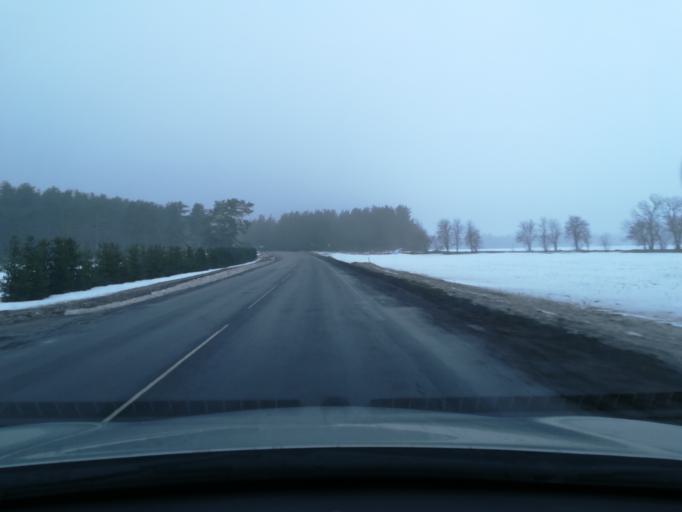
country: EE
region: Harju
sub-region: Raasiku vald
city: Arukula
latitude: 59.3548
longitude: 25.0779
